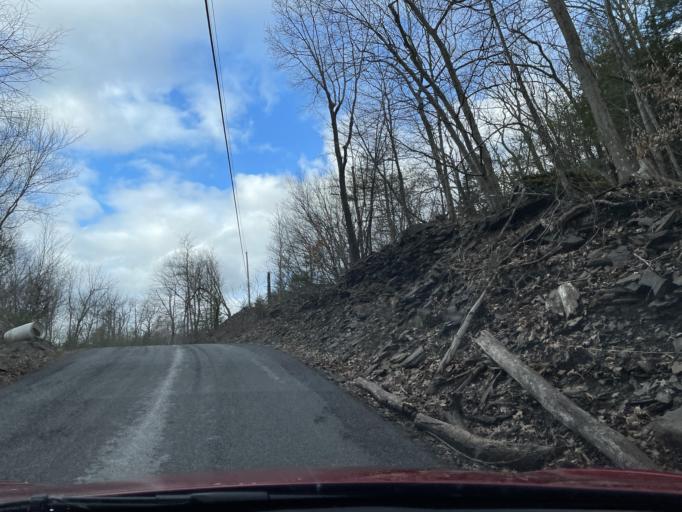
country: US
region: New York
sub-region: Ulster County
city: Zena
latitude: 42.0795
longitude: -74.0584
